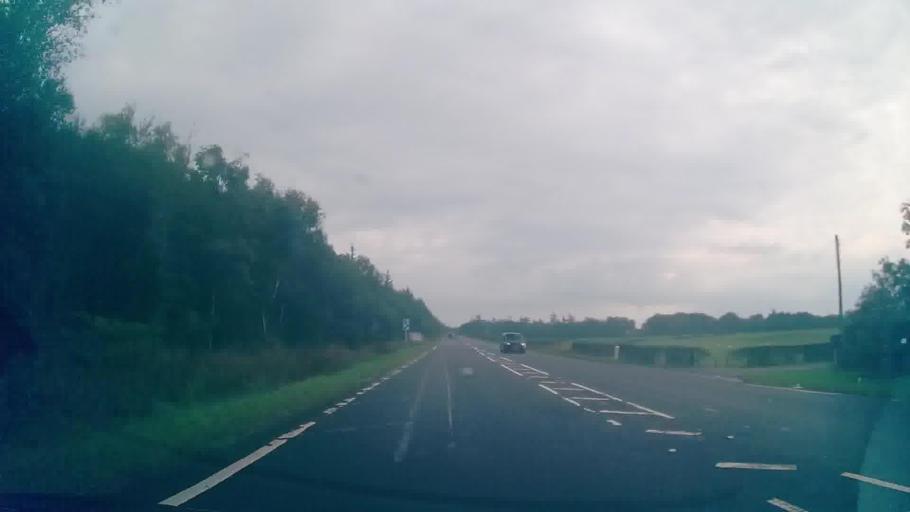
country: GB
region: Scotland
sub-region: Dumfries and Galloway
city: Annan
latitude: 55.0165
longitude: -3.3588
